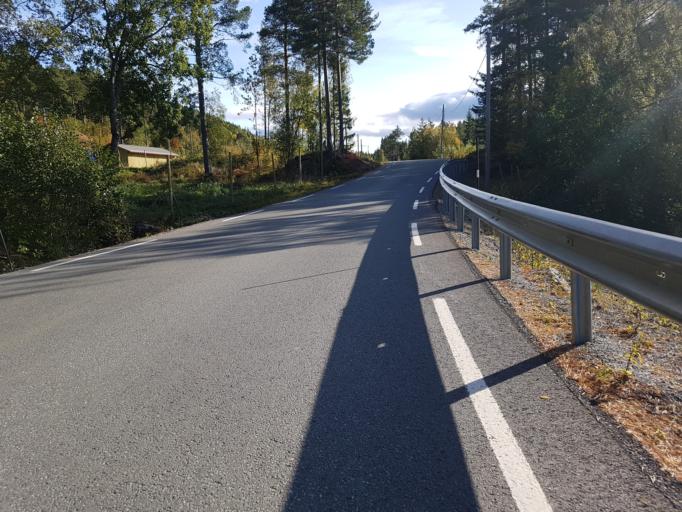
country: NO
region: Sor-Trondelag
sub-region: Malvik
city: Malvik
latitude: 63.3740
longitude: 10.6115
